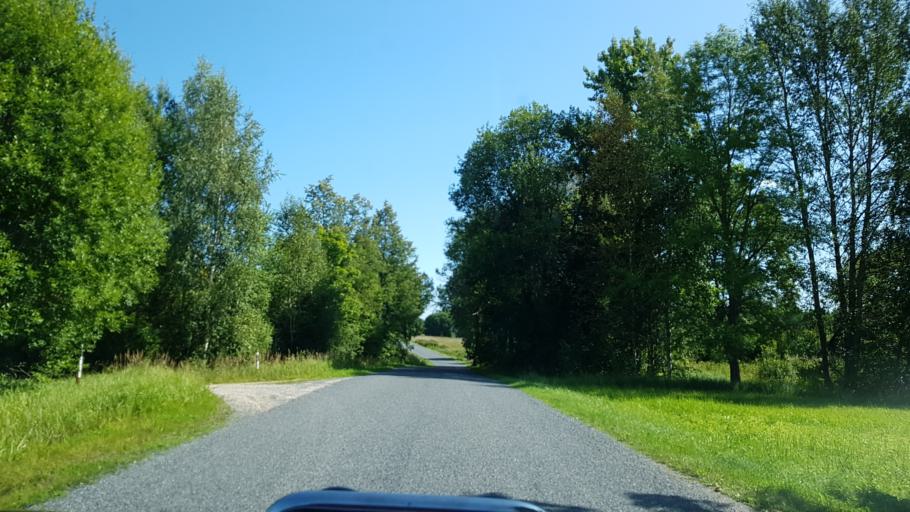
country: EE
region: Vorumaa
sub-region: Voru linn
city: Voru
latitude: 57.7624
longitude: 27.3068
